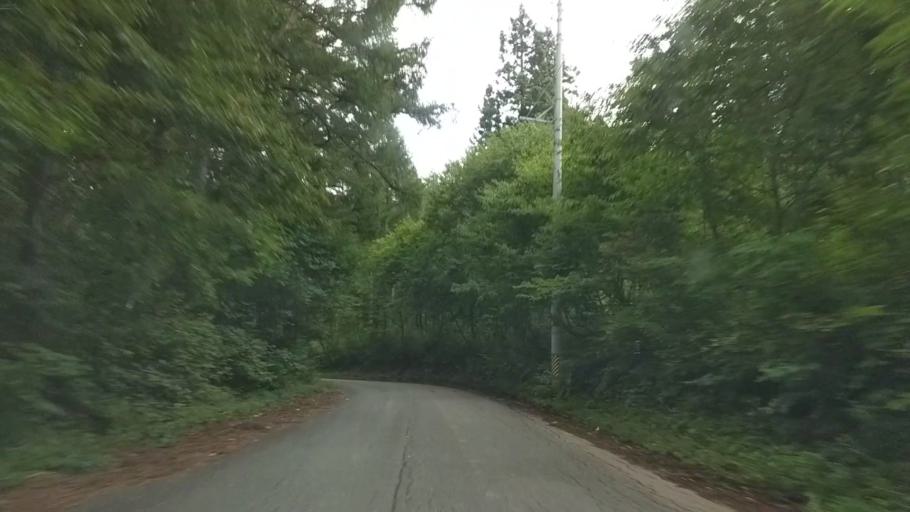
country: JP
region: Nagano
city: Iiyama
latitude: 36.8177
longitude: 138.3831
